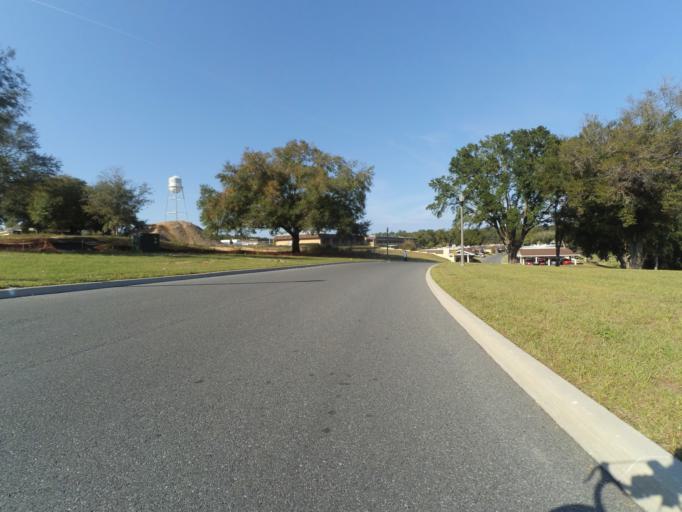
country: US
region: Florida
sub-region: Lake County
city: Umatilla
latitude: 28.9630
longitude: -81.6559
